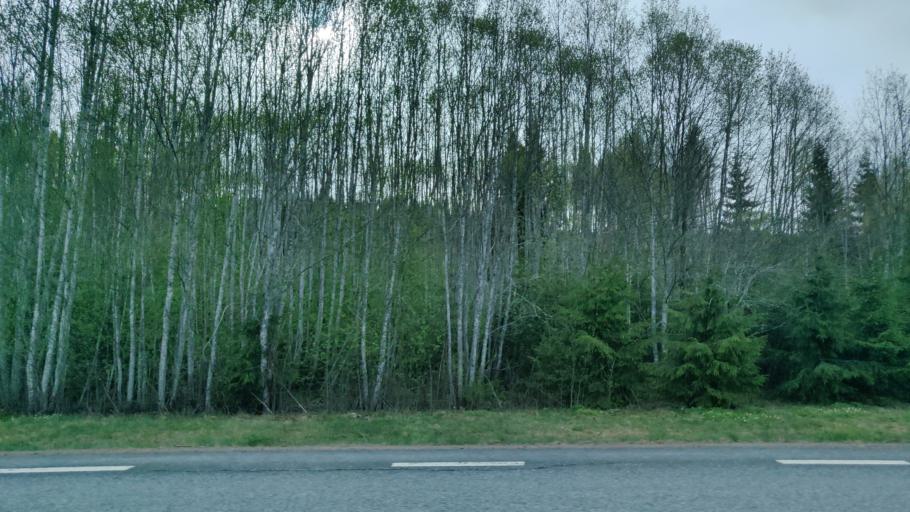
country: SE
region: Vaermland
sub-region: Munkfors Kommun
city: Munkfors
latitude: 59.7690
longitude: 13.4380
